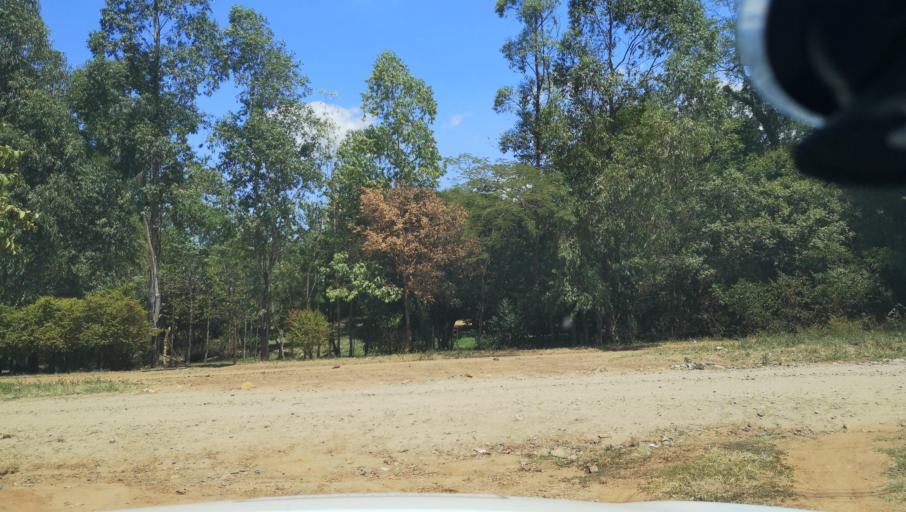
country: PY
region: Itapua
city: Carmen del Parana
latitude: -27.1663
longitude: -56.2489
